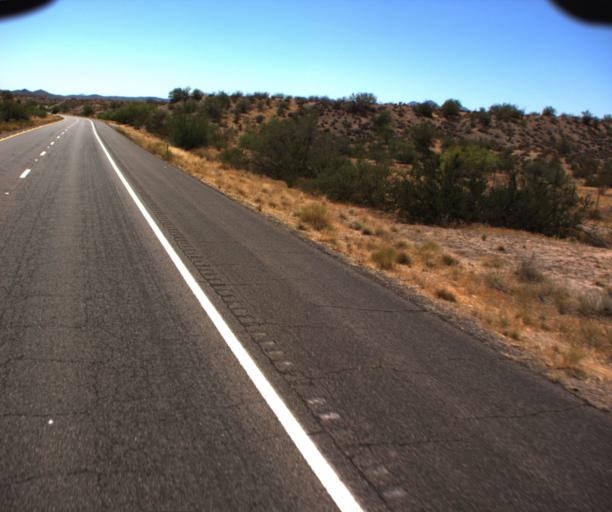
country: US
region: Arizona
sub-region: Maricopa County
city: Fountain Hills
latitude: 33.5831
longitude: -111.6169
